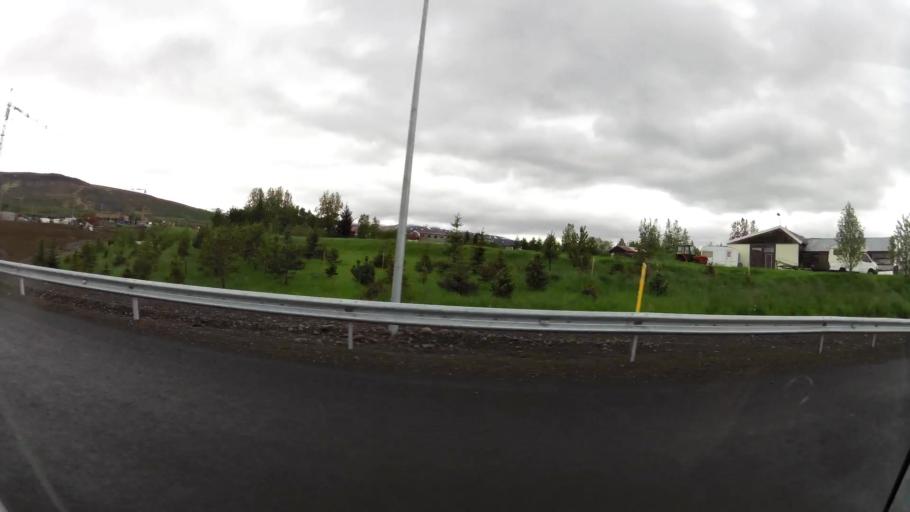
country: IS
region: Northeast
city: Akureyri
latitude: 65.6609
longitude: -18.0902
